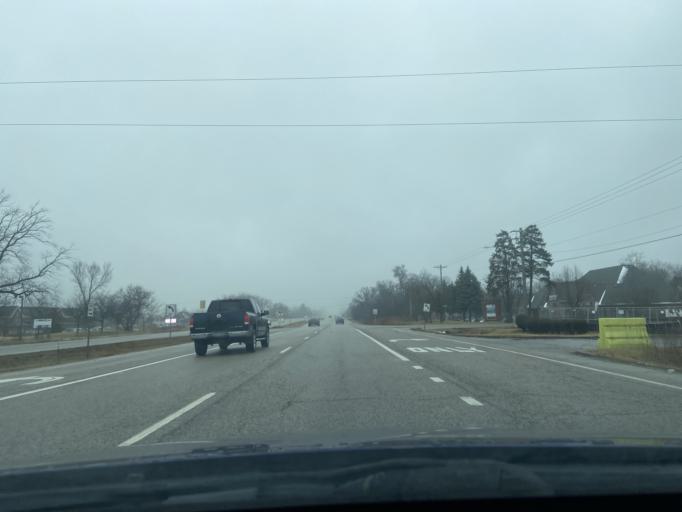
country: US
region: Illinois
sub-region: Lake County
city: Knollwood
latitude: 42.2048
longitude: -88.1114
